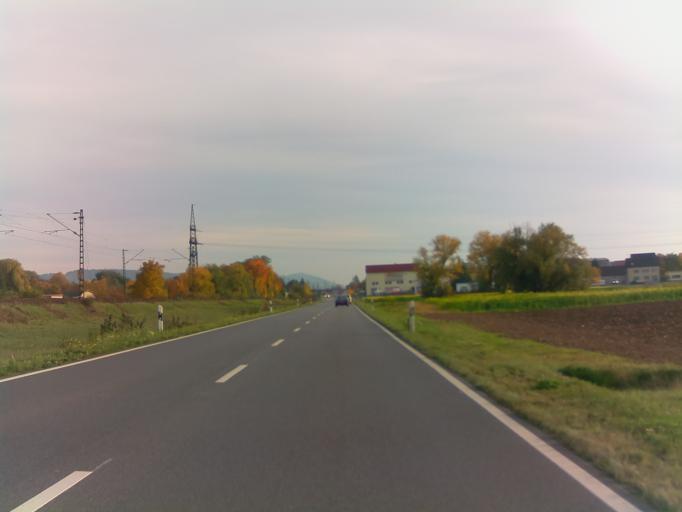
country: DE
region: Baden-Wuerttemberg
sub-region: Karlsruhe Region
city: Hemsbach
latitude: 49.6022
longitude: 8.6461
